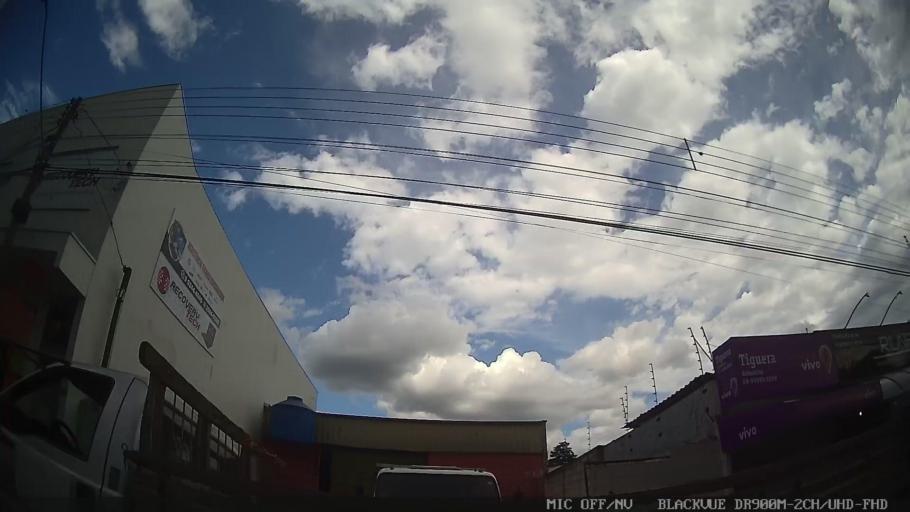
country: BR
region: Sao Paulo
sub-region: Pedreira
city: Pedreira
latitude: -22.7297
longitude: -46.8955
